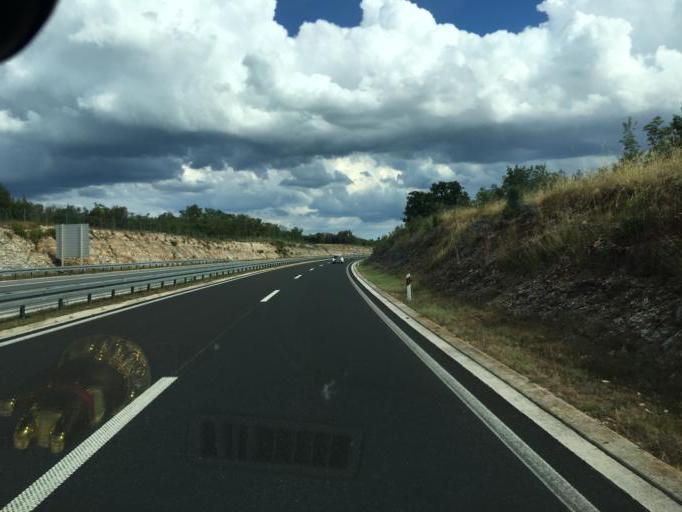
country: HR
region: Istarska
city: Vodnjan
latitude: 45.0254
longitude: 13.8395
